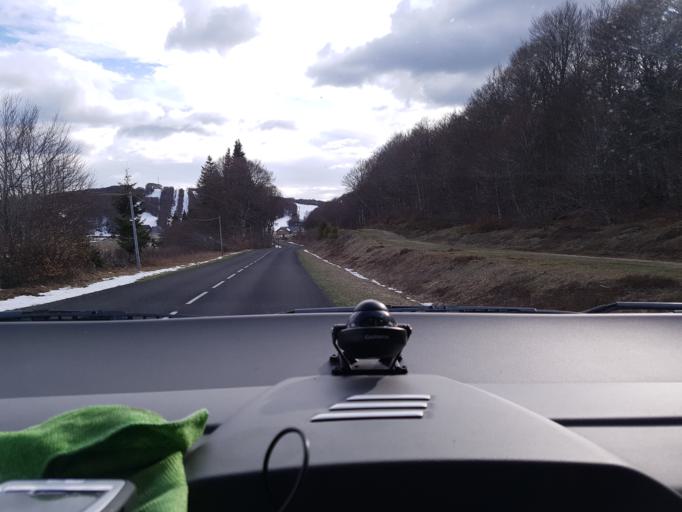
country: FR
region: Midi-Pyrenees
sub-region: Departement de l'Aveyron
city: Laguiole
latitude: 44.6763
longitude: 2.9311
